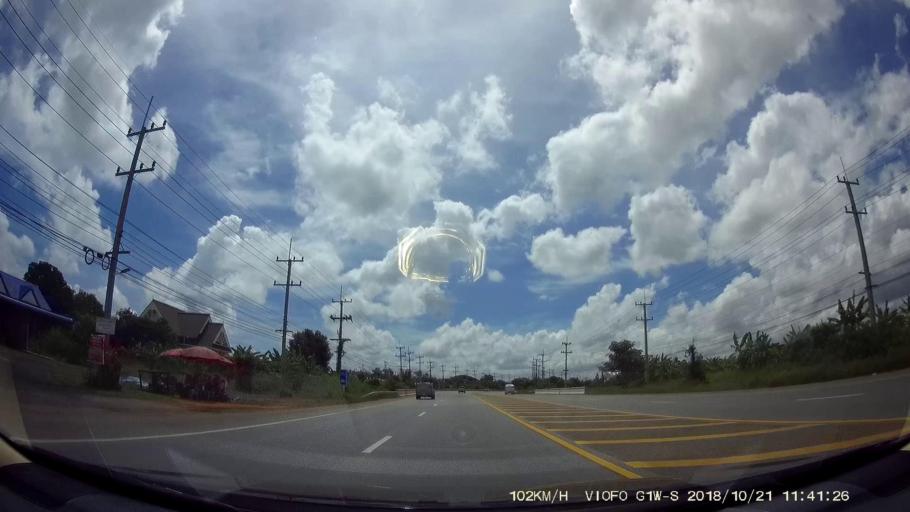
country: TH
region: Chaiyaphum
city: Chaiyaphum
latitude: 15.6988
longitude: 102.0146
